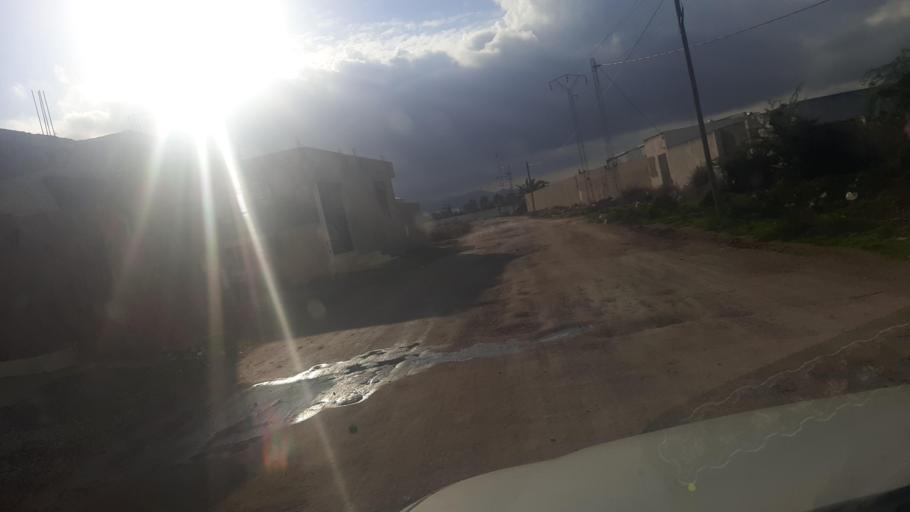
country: TN
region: Nabul
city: Manzil Bu Zalafah
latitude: 36.7111
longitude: 10.4841
